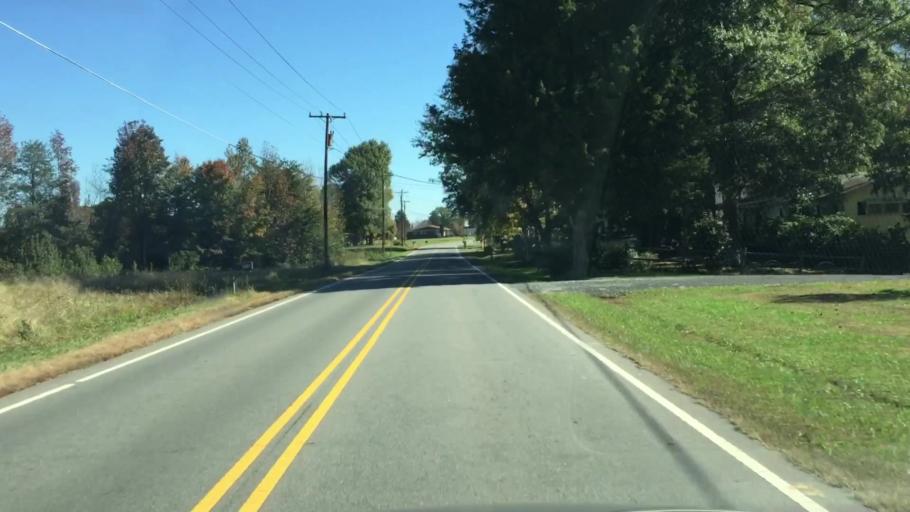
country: US
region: North Carolina
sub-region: Rockingham County
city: Reidsville
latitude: 36.3299
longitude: -79.6202
